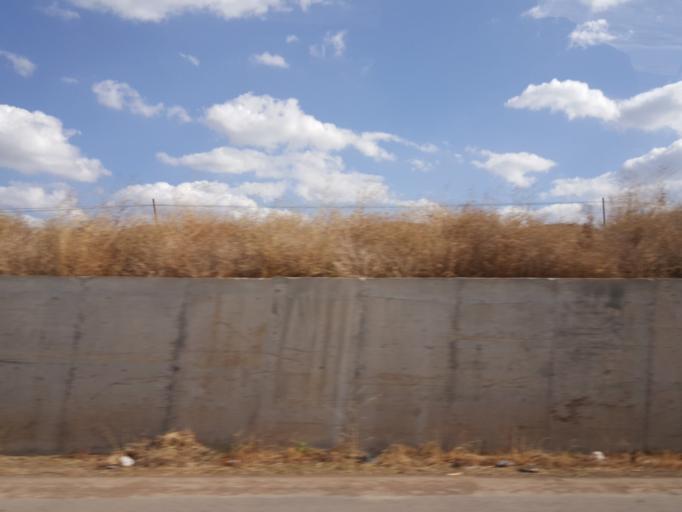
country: TR
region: Tokat
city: Sulusaray
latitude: 39.9835
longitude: 36.0679
